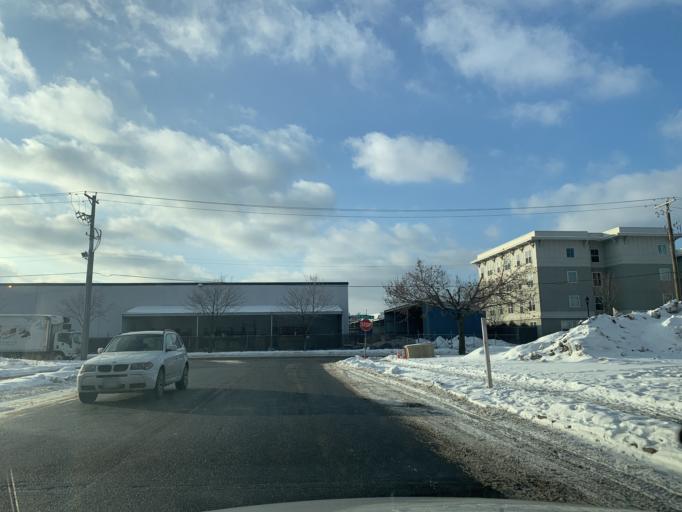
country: US
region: Minnesota
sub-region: Hennepin County
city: Minneapolis
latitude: 44.9808
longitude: -93.2902
